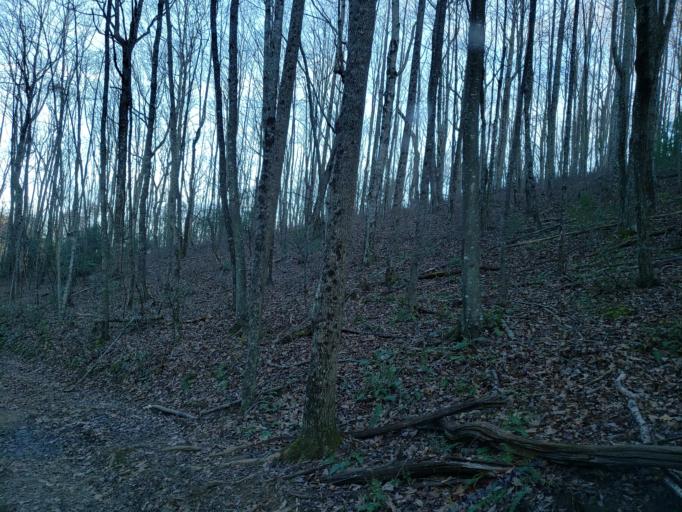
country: US
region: Georgia
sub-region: Lumpkin County
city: Dahlonega
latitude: 34.6677
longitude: -84.1014
